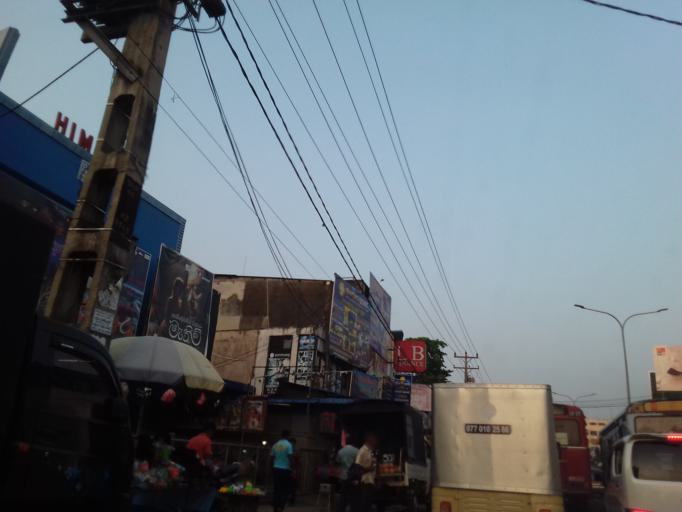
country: LK
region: Western
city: Kelaniya
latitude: 6.9796
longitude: 79.9286
